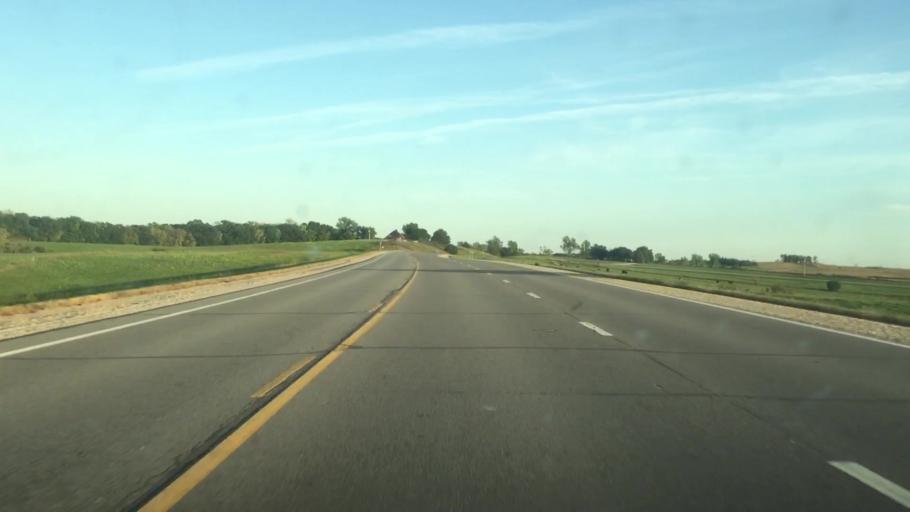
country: US
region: Kansas
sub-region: Atchison County
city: Atchison
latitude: 39.4732
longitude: -95.1004
